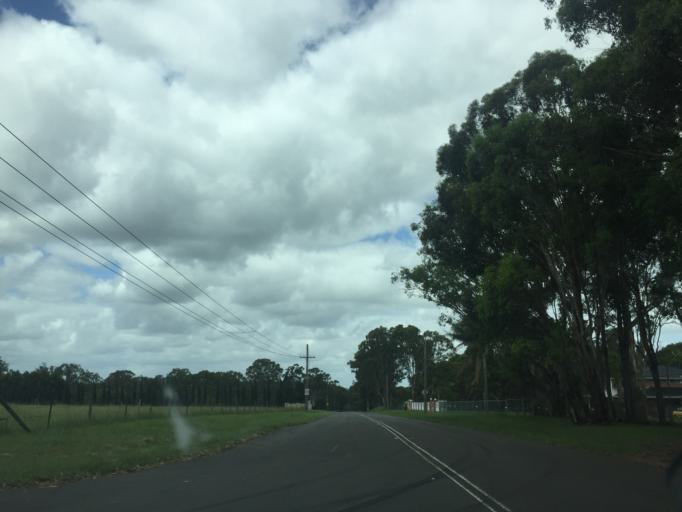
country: AU
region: New South Wales
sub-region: Penrith Municipality
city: Kingswood Park
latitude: -33.7965
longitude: 150.7189
